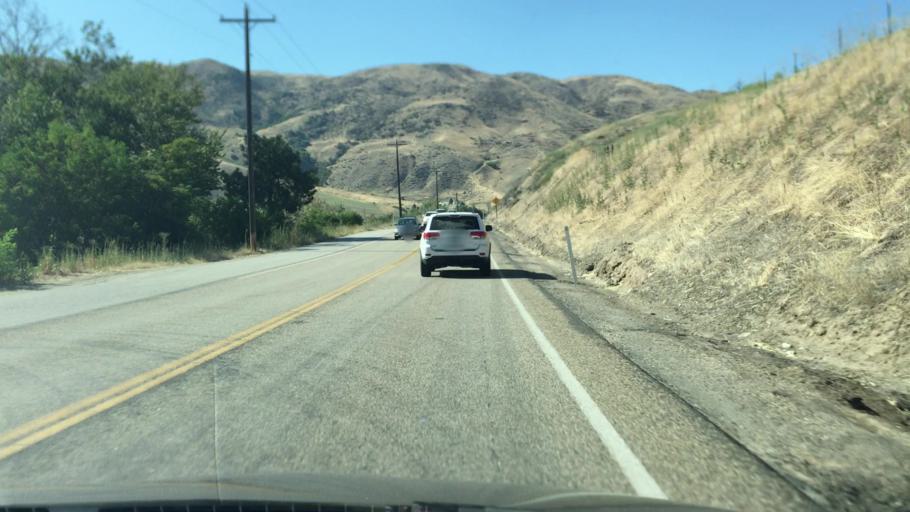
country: US
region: Idaho
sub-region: Ada County
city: Eagle
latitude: 43.9757
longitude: -116.1914
